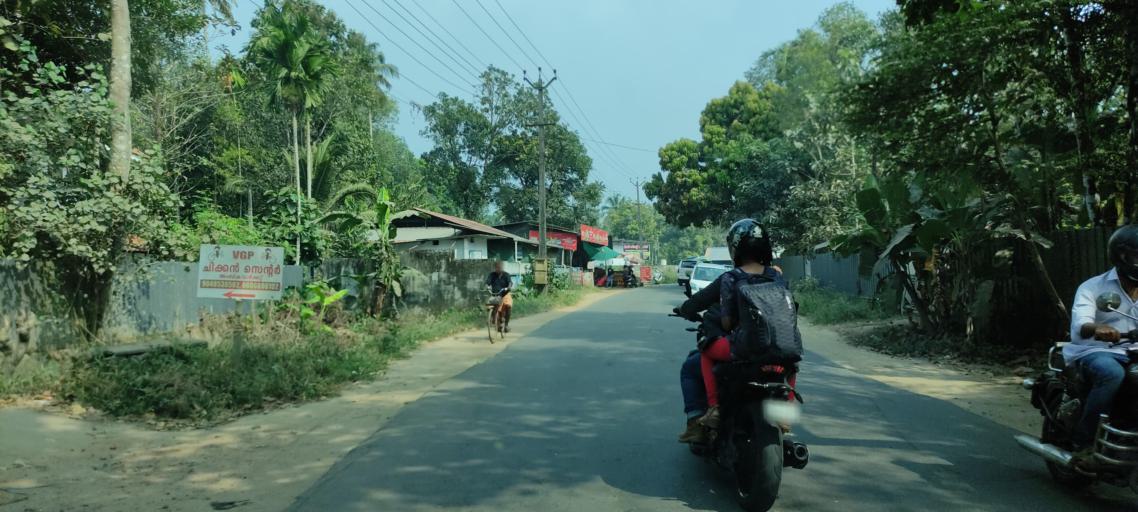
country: IN
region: Kerala
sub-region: Alappuzha
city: Shertallai
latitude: 9.6716
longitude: 76.4109
